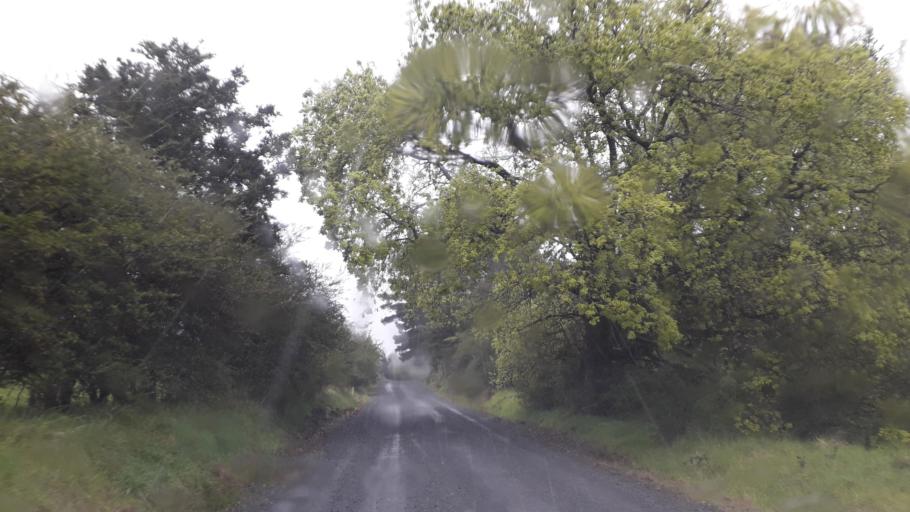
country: NZ
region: Northland
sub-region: Far North District
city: Waimate North
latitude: -35.4875
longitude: 173.7009
